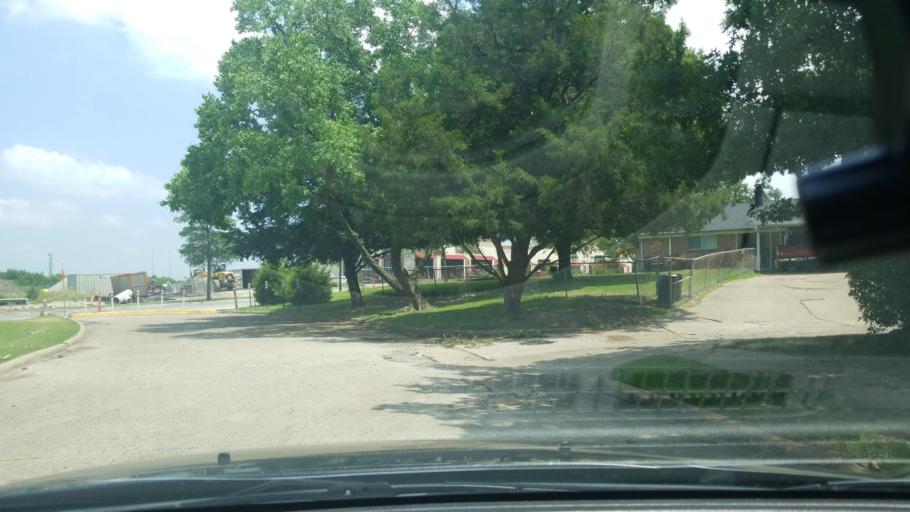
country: US
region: Texas
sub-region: Dallas County
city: Mesquite
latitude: 32.8012
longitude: -96.6343
